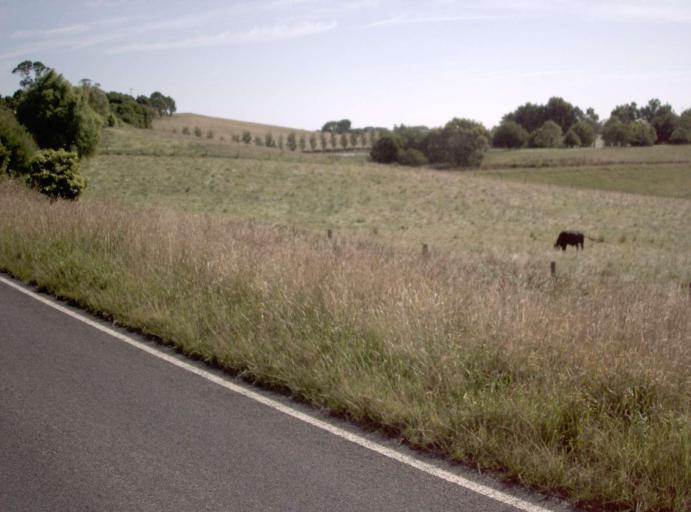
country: AU
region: Victoria
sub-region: Baw Baw
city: Warragul
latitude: -38.3167
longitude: 145.7721
